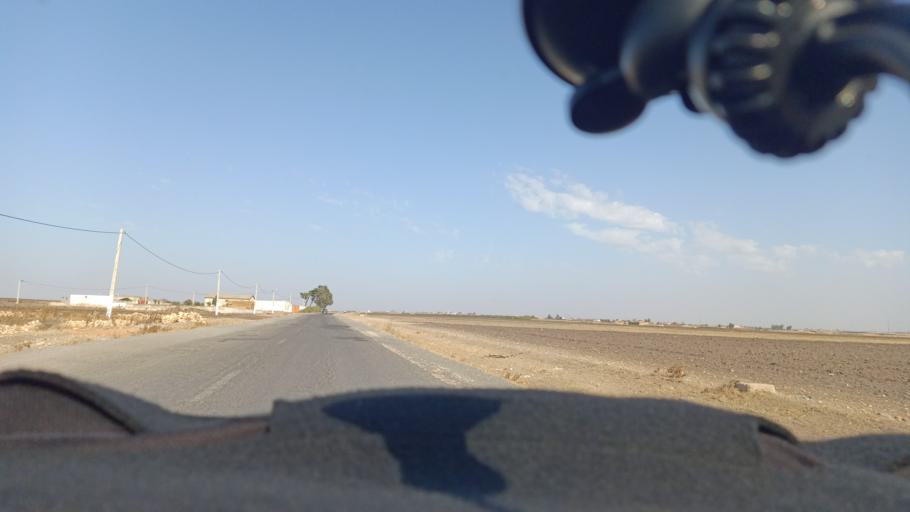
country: MA
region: Doukkala-Abda
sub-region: Safi
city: Youssoufia
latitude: 32.3711
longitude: -8.7203
